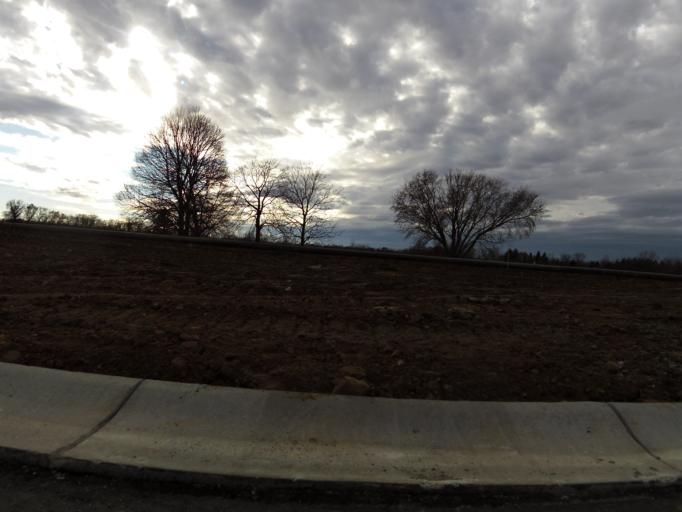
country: US
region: Minnesota
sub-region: Washington County
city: Lake Elmo
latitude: 44.9726
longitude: -92.8638
